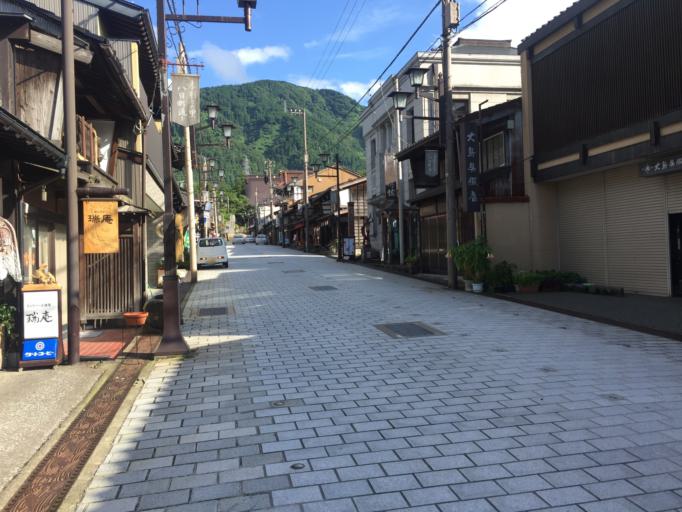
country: JP
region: Toyama
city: Nanto-shi
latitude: 36.5606
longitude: 136.9709
